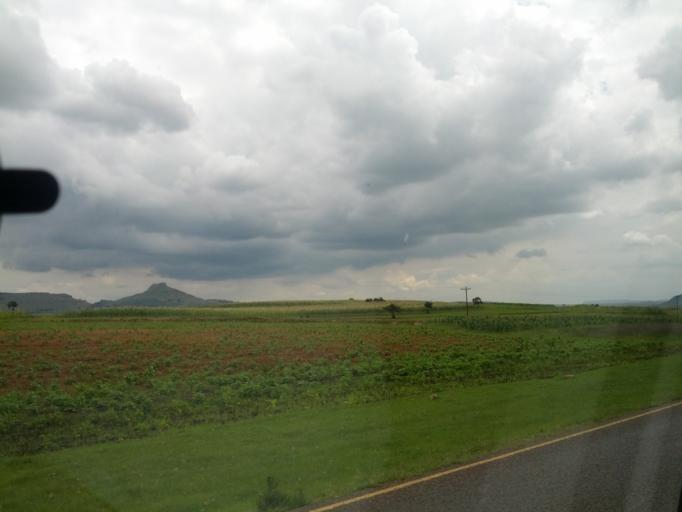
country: LS
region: Leribe
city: Leribe
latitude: -28.9772
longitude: 28.1776
